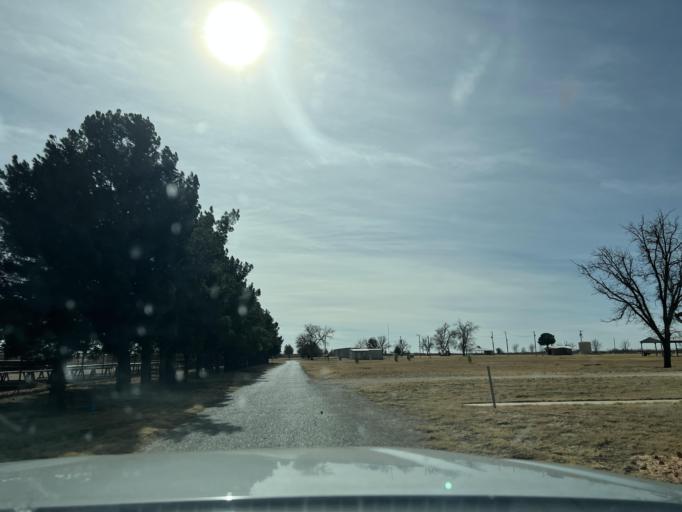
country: US
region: Texas
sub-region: Andrews County
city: Andrews
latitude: 32.4563
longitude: -102.5696
